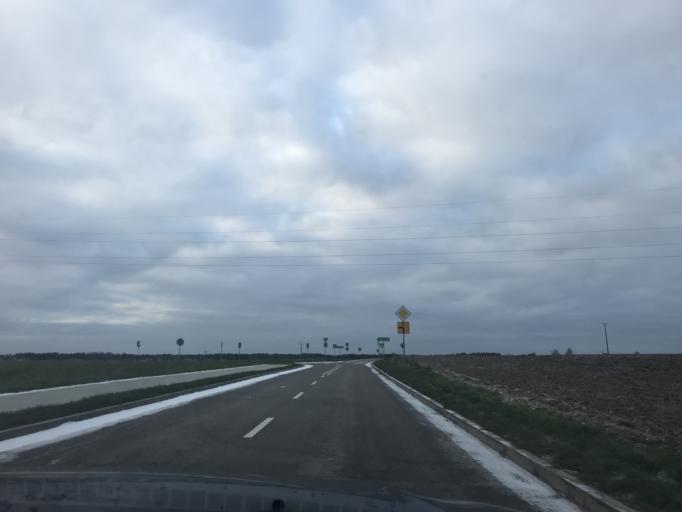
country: PL
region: Pomeranian Voivodeship
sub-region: Powiat chojnicki
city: Brusy
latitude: 53.8719
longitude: 17.7521
